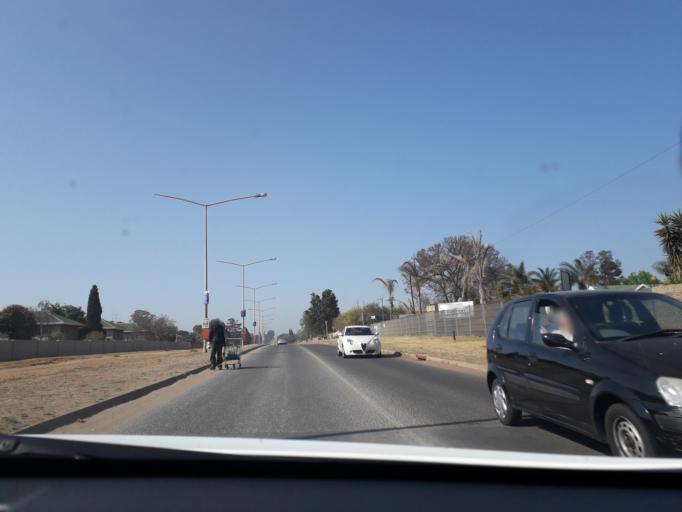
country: ZA
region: Gauteng
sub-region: City of Johannesburg Metropolitan Municipality
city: Modderfontein
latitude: -26.0803
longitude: 28.2482
